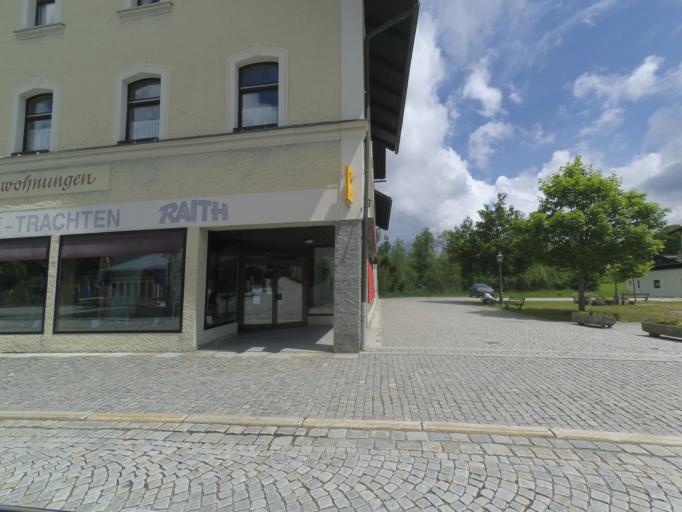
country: DE
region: Bavaria
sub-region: Lower Bavaria
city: Bayerisch Eisenstein
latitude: 49.1211
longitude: 13.2029
